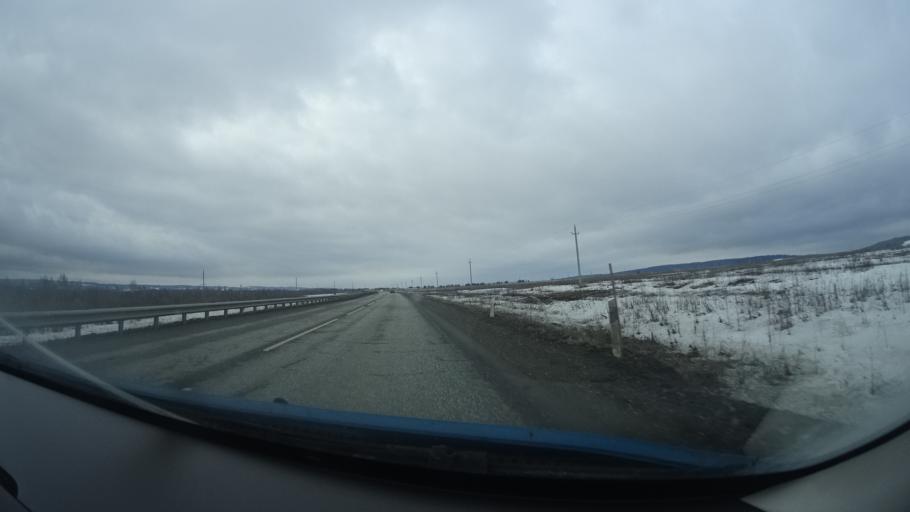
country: RU
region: Perm
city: Barda
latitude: 56.9618
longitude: 55.5793
